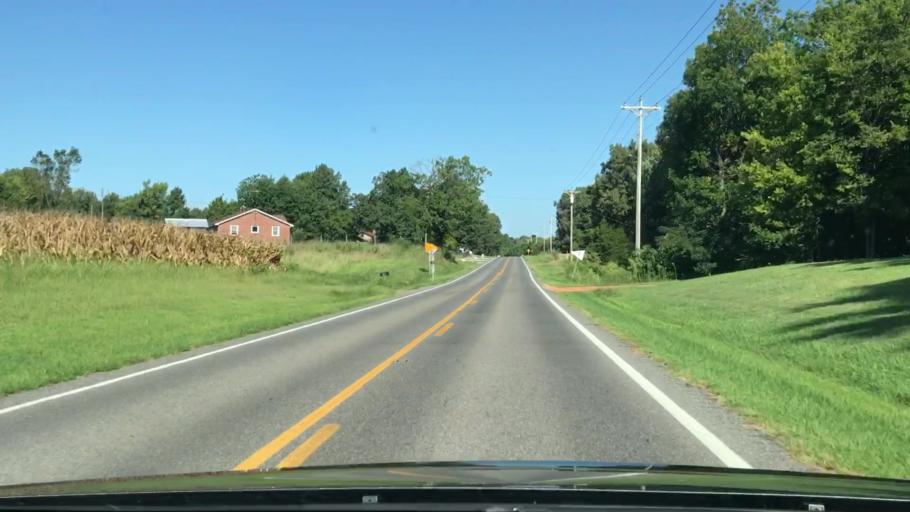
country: US
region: Kentucky
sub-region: Graves County
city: Mayfield
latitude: 36.7757
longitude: -88.5065
